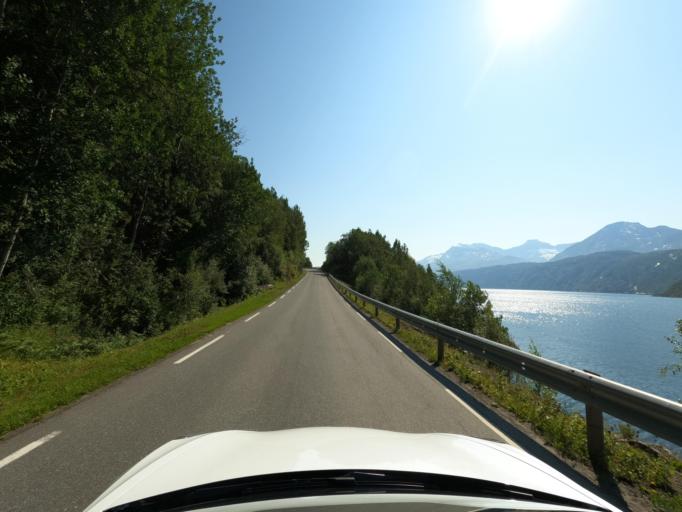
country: NO
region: Nordland
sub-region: Narvik
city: Narvik
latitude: 68.3616
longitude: 17.2627
